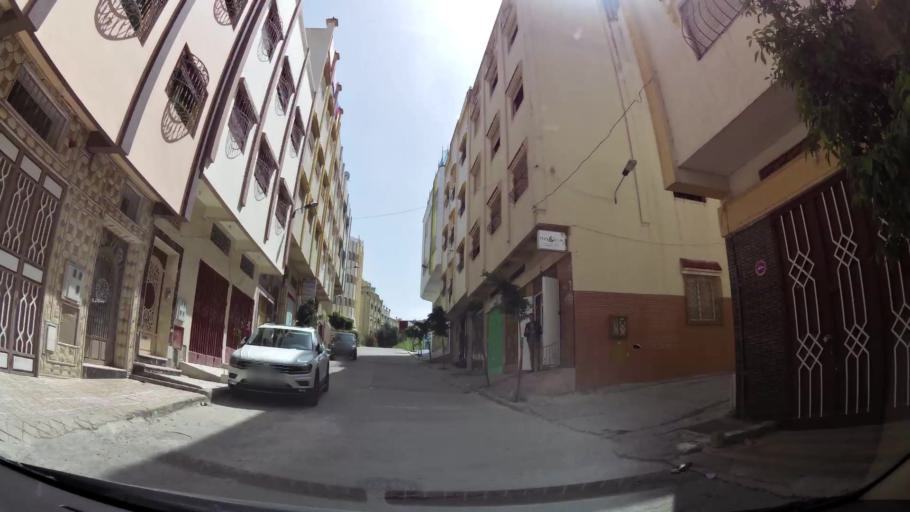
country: MA
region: Tanger-Tetouan
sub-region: Tanger-Assilah
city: Tangier
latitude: 35.7605
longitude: -5.8371
